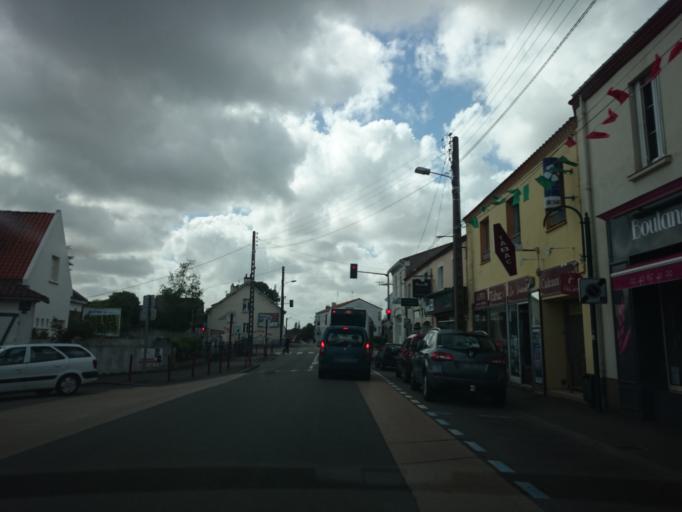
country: FR
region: Pays de la Loire
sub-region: Departement de la Loire-Atlantique
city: Bouaye
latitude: 47.1439
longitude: -1.6924
